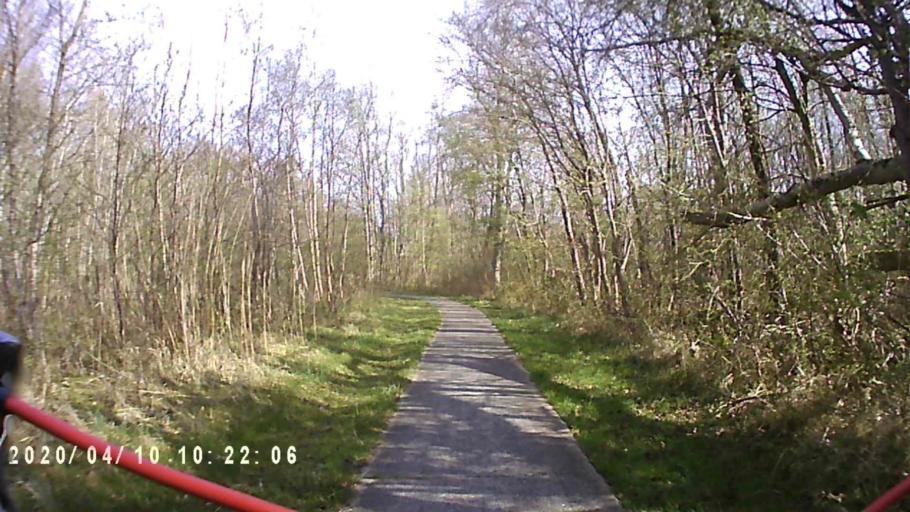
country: NL
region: Friesland
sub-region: Gemeente Dongeradeel
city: Anjum
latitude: 53.3825
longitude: 6.2158
